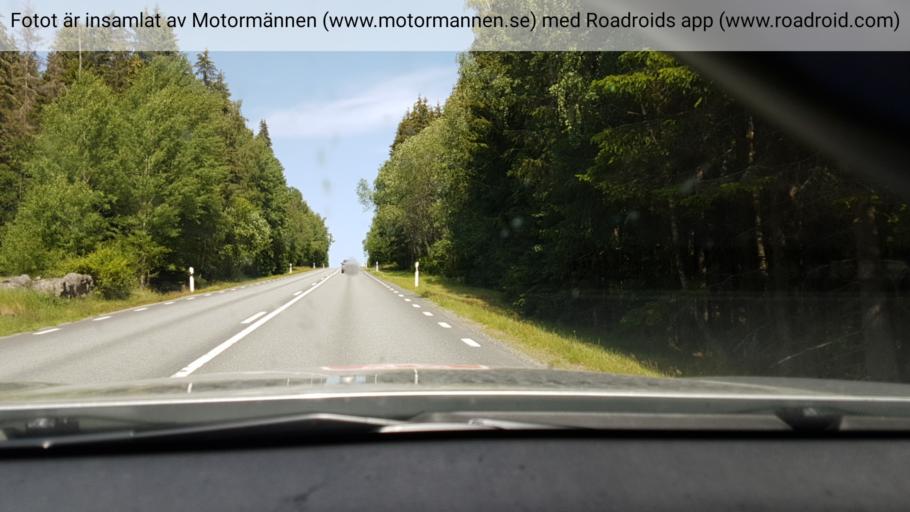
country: SE
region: Joenkoeping
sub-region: Nassjo Kommun
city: Nassjo
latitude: 57.5866
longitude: 14.8257
